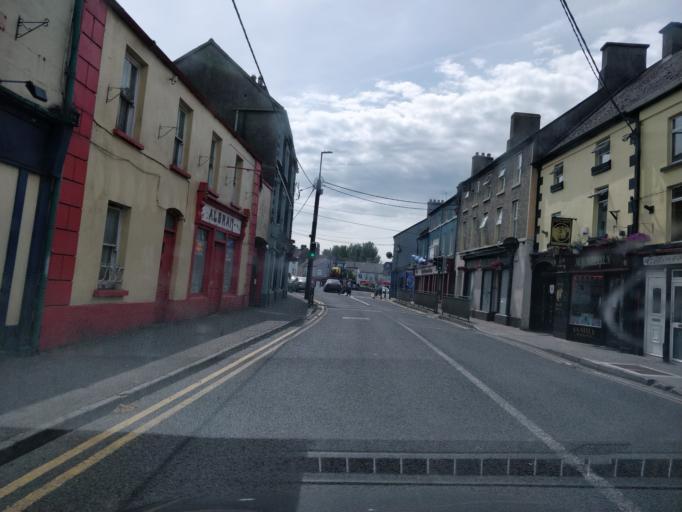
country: IE
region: Leinster
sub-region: Laois
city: Mountrath
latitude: 53.0021
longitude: -7.4749
